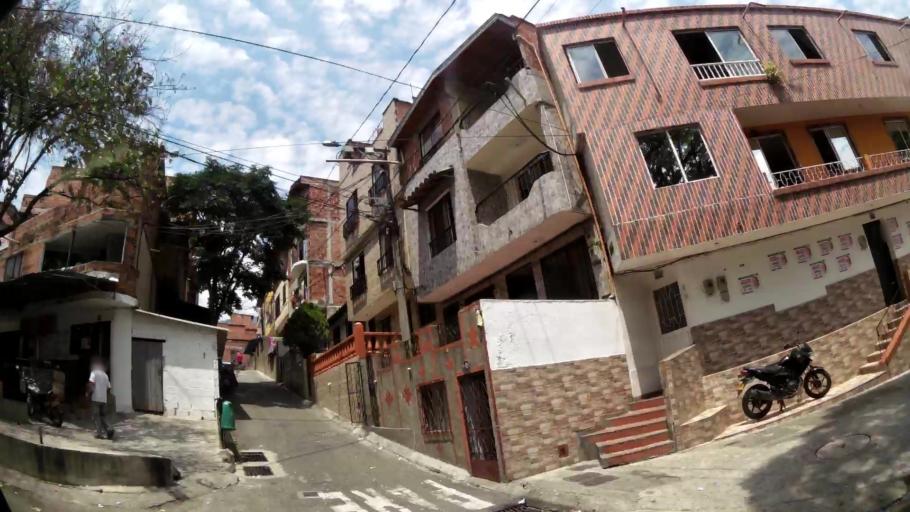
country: CO
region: Antioquia
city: Bello
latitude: 6.3126
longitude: -75.5697
